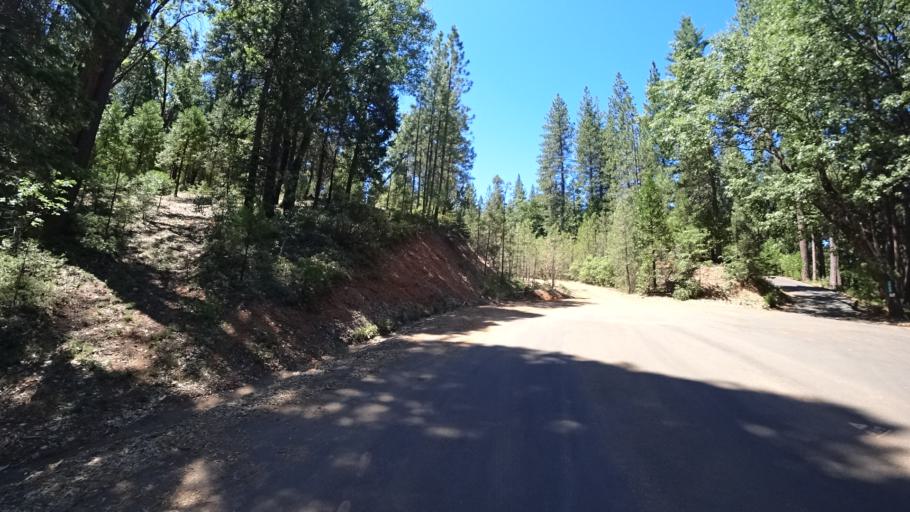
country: US
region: California
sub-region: Calaveras County
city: Arnold
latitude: 38.2304
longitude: -120.3463
